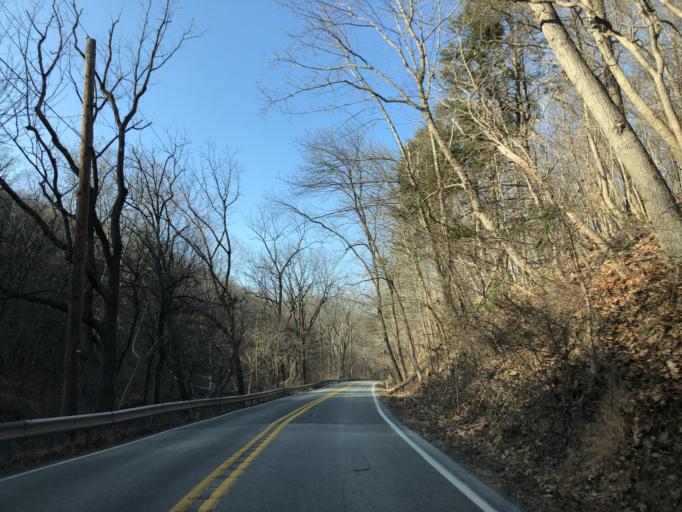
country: US
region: Pennsylvania
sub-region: Chester County
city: Chesterbrook
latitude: 40.0958
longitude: -75.4595
